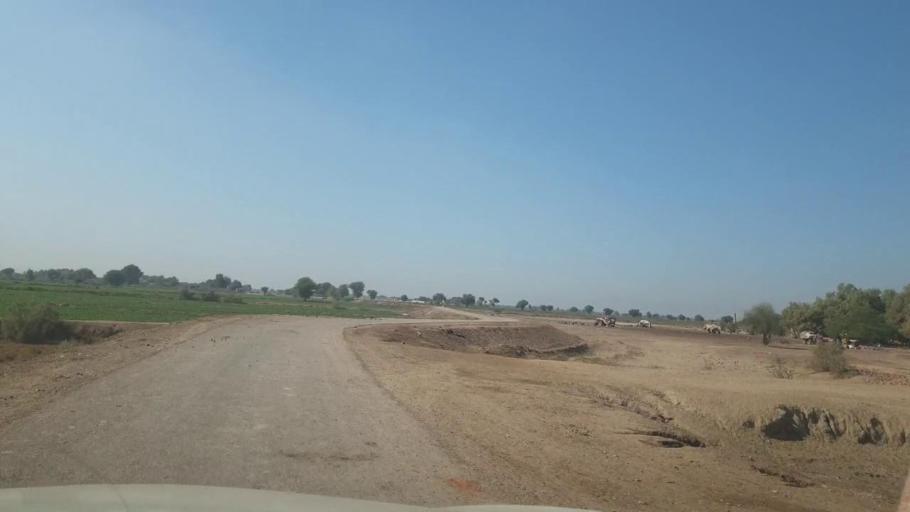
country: PK
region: Sindh
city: Bhan
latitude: 26.5661
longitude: 67.7029
